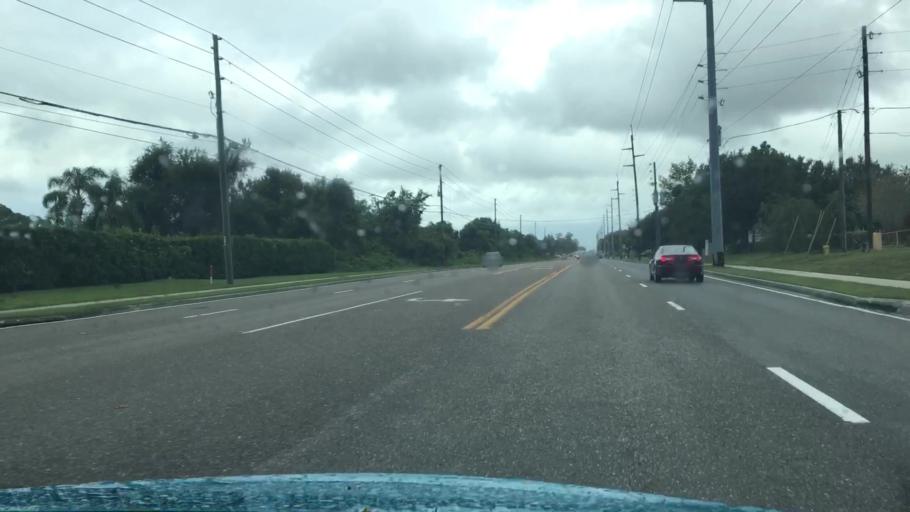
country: US
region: Florida
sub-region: Volusia County
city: Deltona
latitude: 28.8944
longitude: -81.2831
